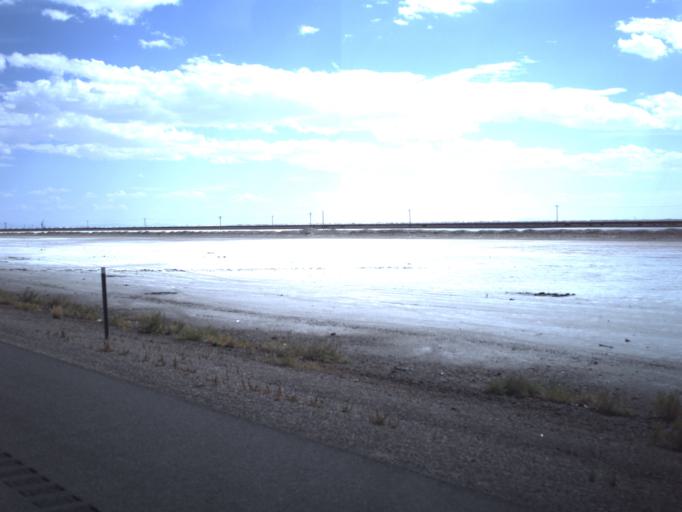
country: US
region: Utah
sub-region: Tooele County
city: Wendover
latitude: 40.7398
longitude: -113.9211
